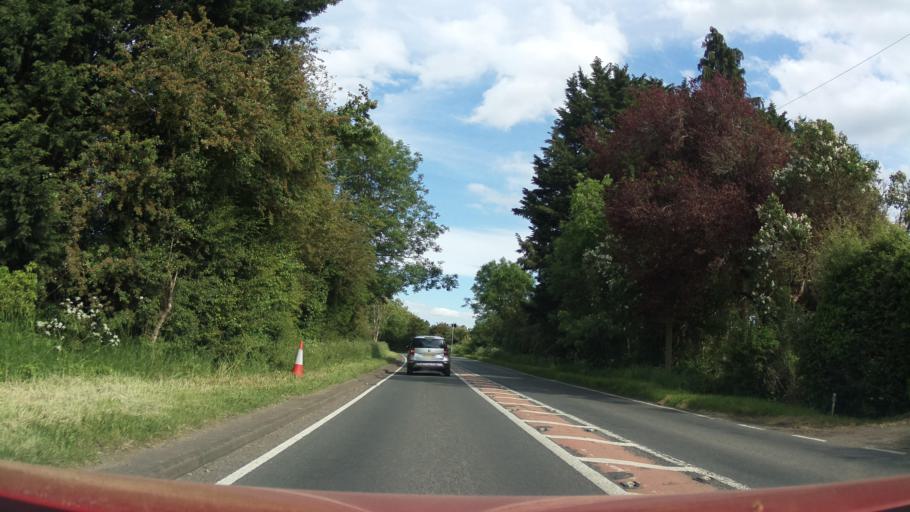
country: GB
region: England
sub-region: Worcestershire
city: Evesham
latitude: 52.0949
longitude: -2.0022
